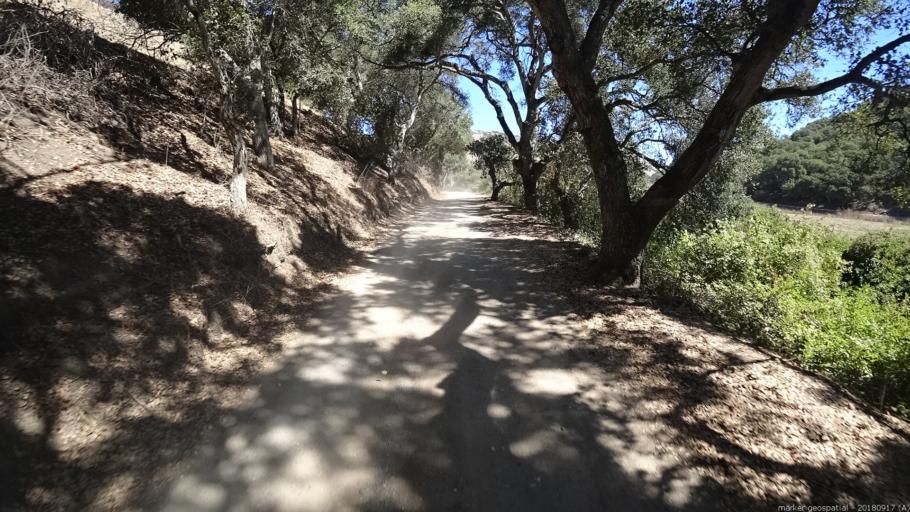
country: US
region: California
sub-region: San Benito County
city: San Juan Bautista
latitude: 36.8039
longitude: -121.5643
